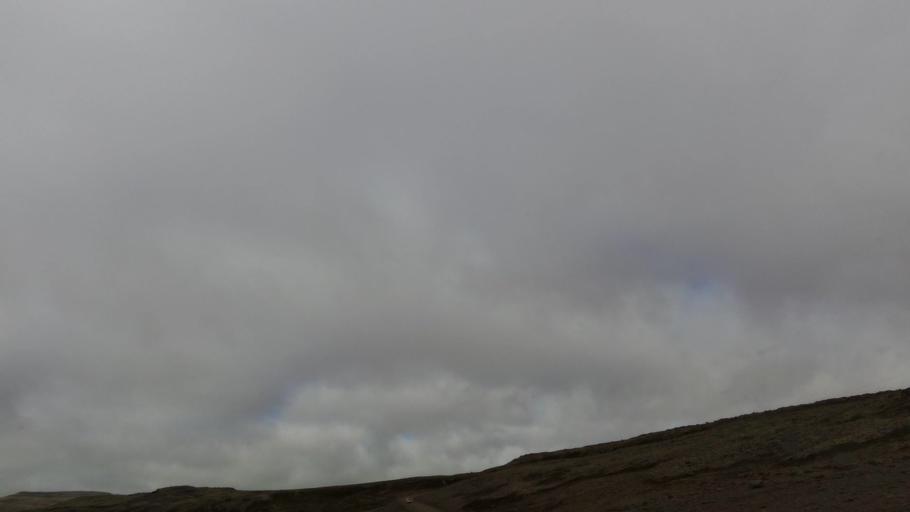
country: IS
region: West
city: Olafsvik
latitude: 65.5443
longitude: -24.3458
